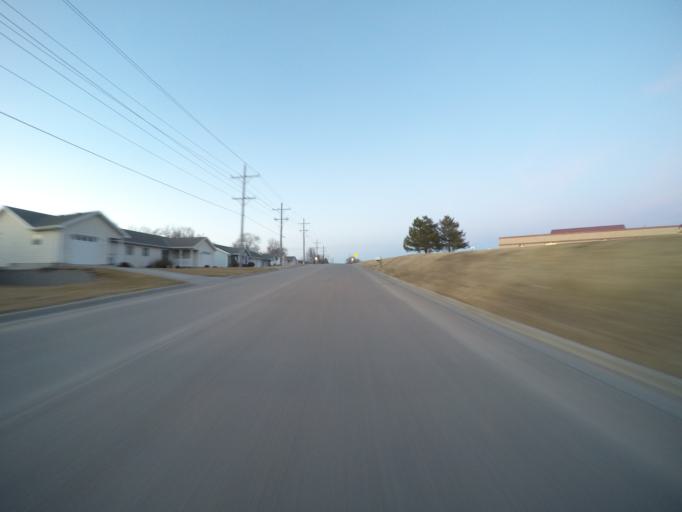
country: US
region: Kansas
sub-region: Clay County
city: Clay Center
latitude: 39.3882
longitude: -97.1188
